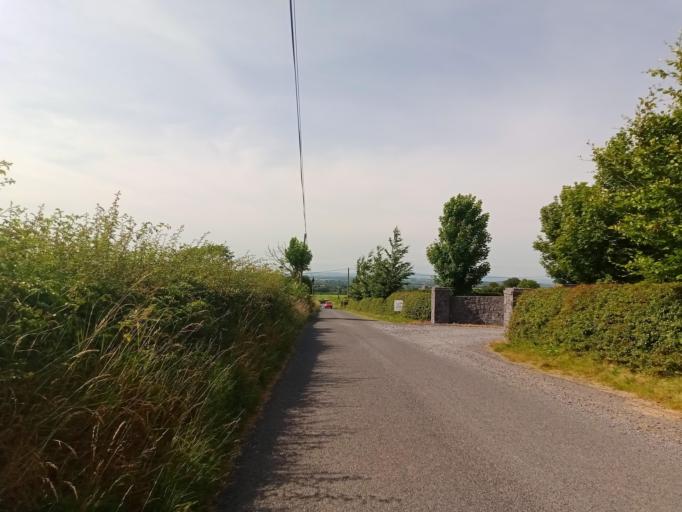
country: IE
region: Leinster
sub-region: Laois
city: Rathdowney
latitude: 52.8067
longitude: -7.4656
